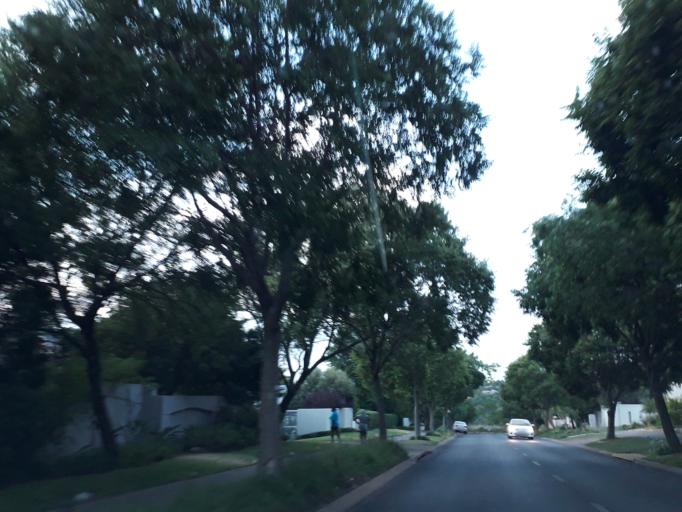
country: ZA
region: Gauteng
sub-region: City of Johannesburg Metropolitan Municipality
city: Diepsloot
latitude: -25.9892
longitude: 28.0033
